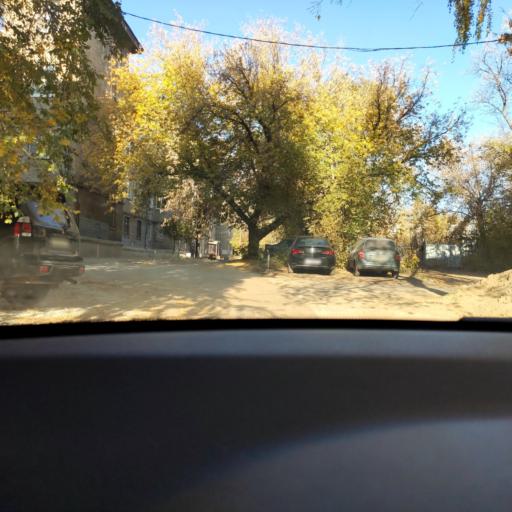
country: RU
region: Samara
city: Samara
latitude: 53.2057
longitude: 50.2321
